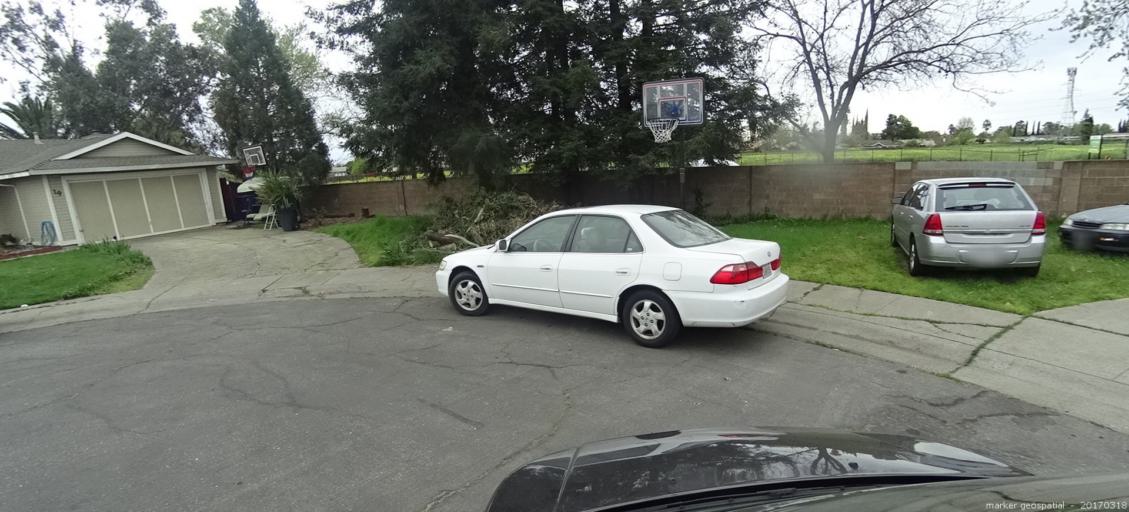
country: US
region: California
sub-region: Sacramento County
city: Parkway
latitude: 38.4756
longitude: -121.4589
